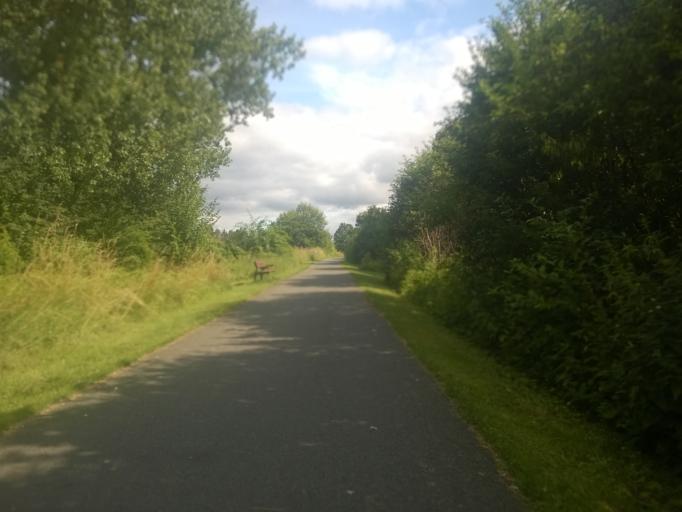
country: SE
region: Skane
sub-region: Kristianstads Kommun
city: Kristianstad
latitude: 56.0497
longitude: 14.1674
